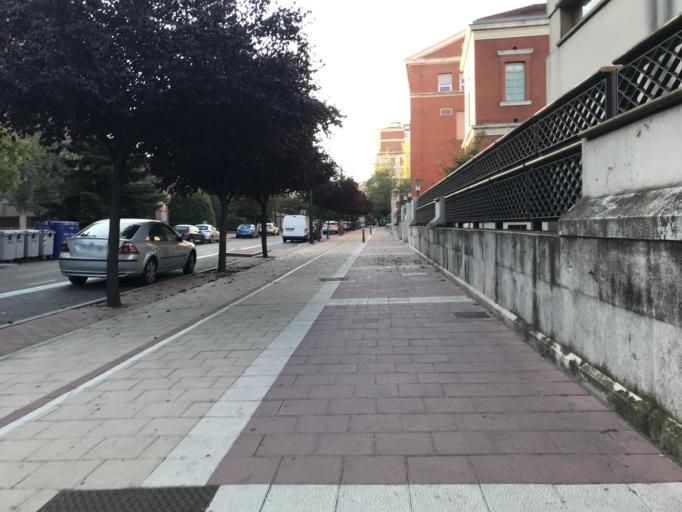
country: ES
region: Castille and Leon
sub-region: Provincia de Valladolid
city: Valladolid
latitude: 41.6556
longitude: -4.7170
